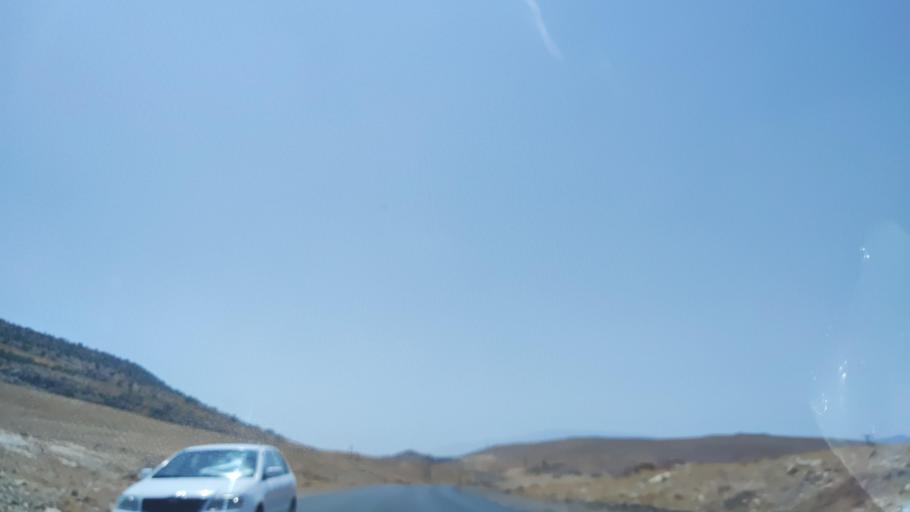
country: IQ
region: Arbil
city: Shaqlawah
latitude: 36.5918
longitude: 44.3197
